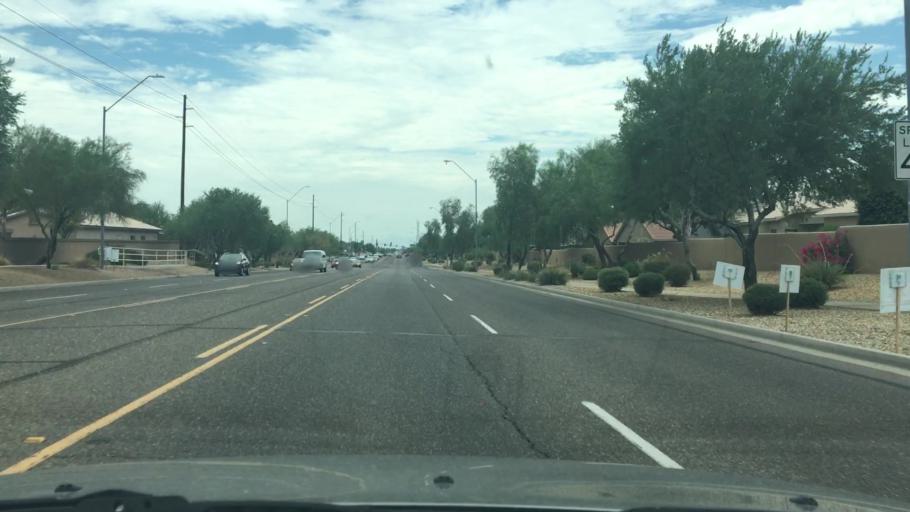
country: US
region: Arizona
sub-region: Maricopa County
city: Sun City
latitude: 33.7167
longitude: -112.2032
